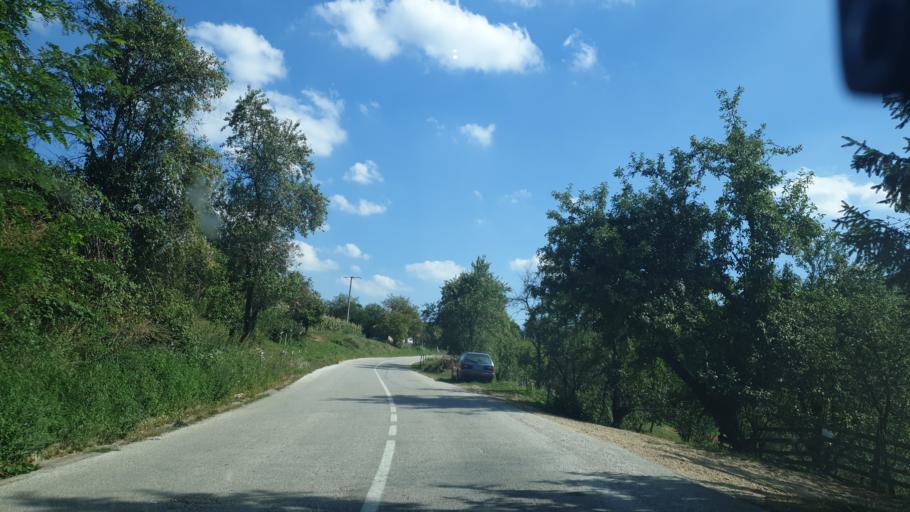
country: RS
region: Central Serbia
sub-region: Zlatiborski Okrug
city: Kosjeric
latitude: 44.0084
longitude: 20.0474
